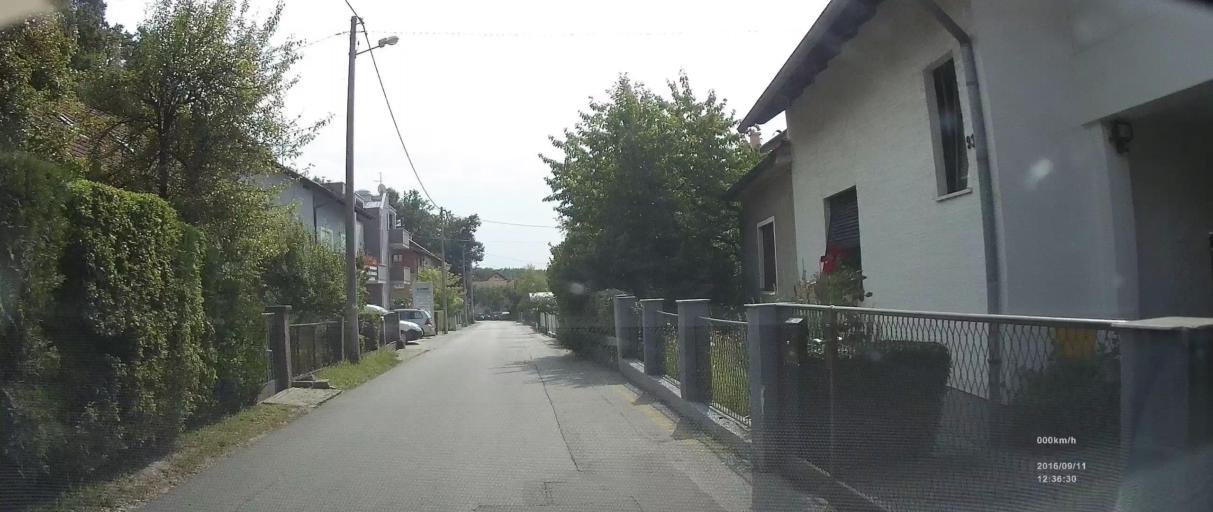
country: HR
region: Grad Zagreb
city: Zagreb
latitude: 45.8352
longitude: 16.0127
